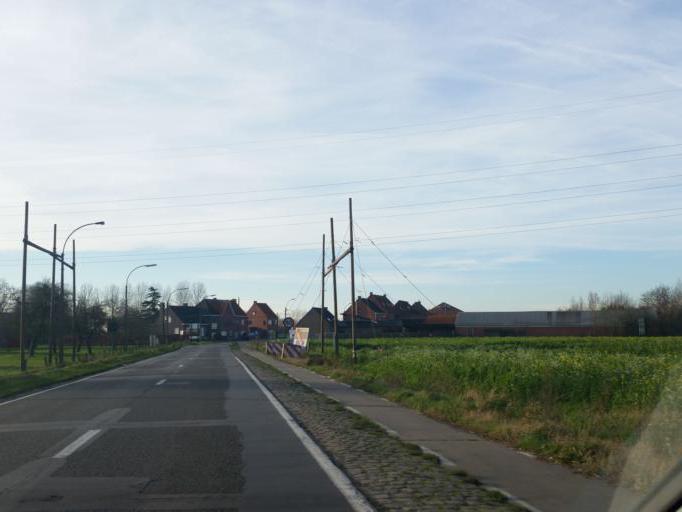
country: BE
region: Flanders
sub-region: Provincie Oost-Vlaanderen
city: Eeklo
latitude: 51.1721
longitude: 3.5431
